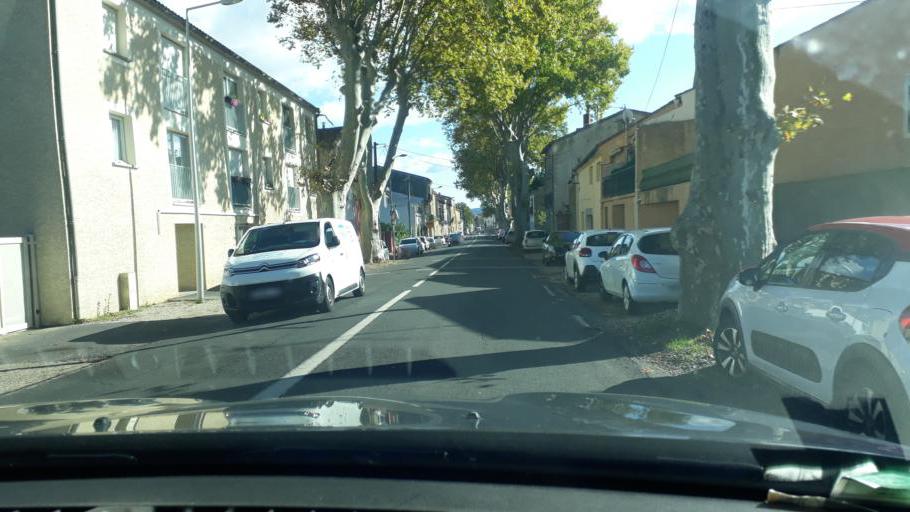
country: FR
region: Languedoc-Roussillon
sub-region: Departement de l'Herault
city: Saint-Andre-de-Sangonis
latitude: 43.6509
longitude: 3.4996
